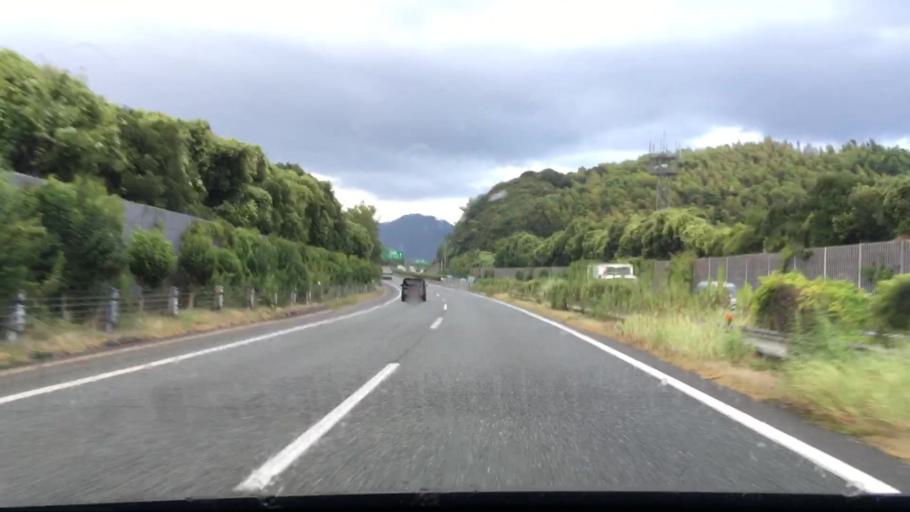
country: JP
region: Fukuoka
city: Kitakyushu
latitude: 33.8071
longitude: 130.8773
